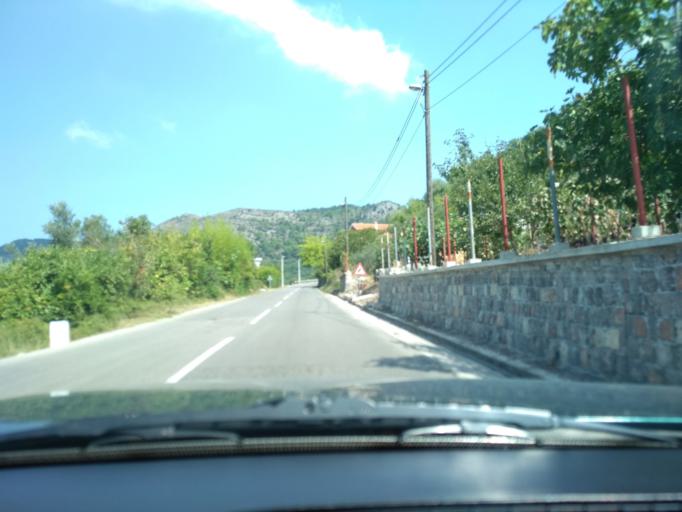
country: ME
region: Kotor
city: Kotor
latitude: 42.3961
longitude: 18.7553
